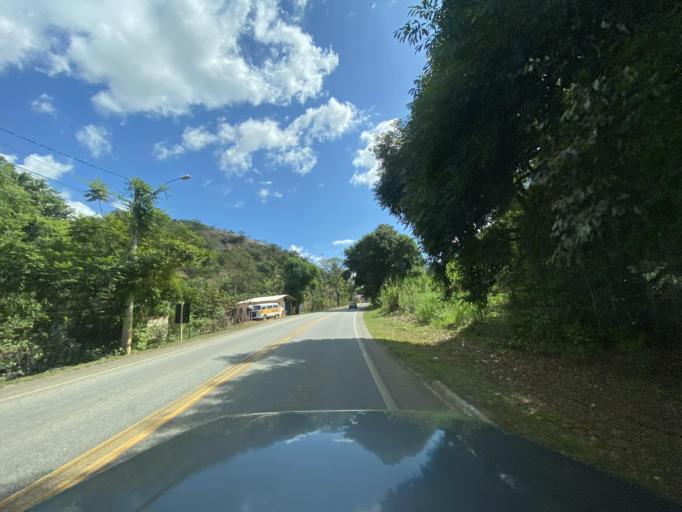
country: BR
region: Espirito Santo
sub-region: Jeronimo Monteiro
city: Jeronimo Monteiro
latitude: -20.7678
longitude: -41.4444
